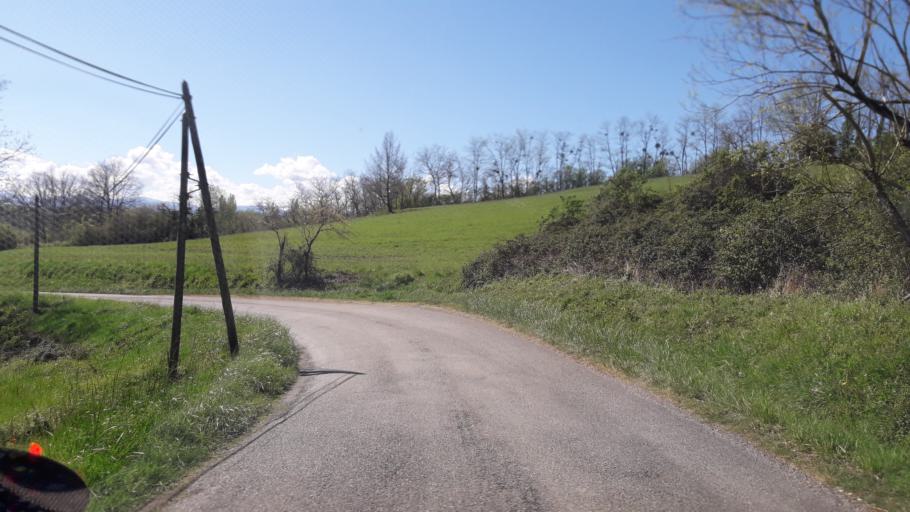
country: FR
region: Midi-Pyrenees
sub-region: Departement de la Haute-Garonne
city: Montesquieu-Volvestre
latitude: 43.1633
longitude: 1.3182
